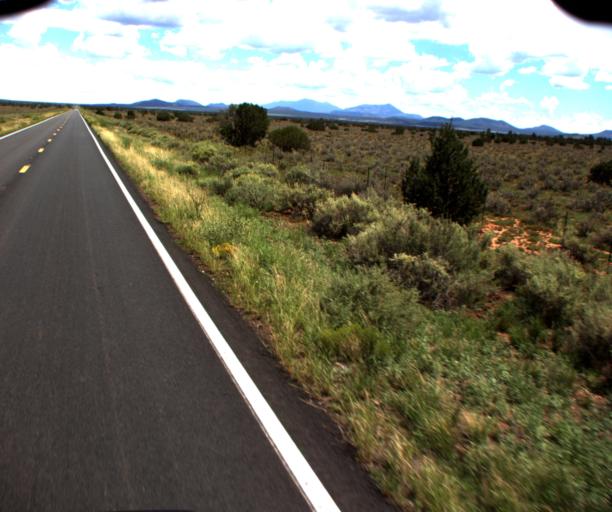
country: US
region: Arizona
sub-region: Coconino County
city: Williams
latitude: 35.6208
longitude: -112.1024
